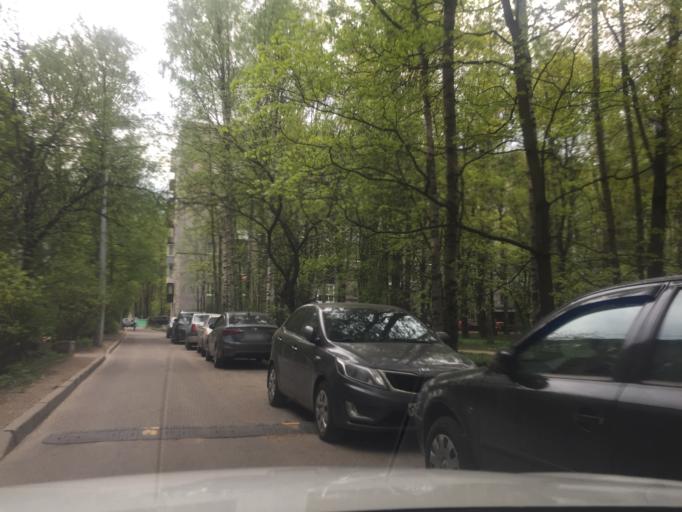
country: RU
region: Leningrad
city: Akademicheskoe
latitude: 60.0052
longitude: 30.3949
